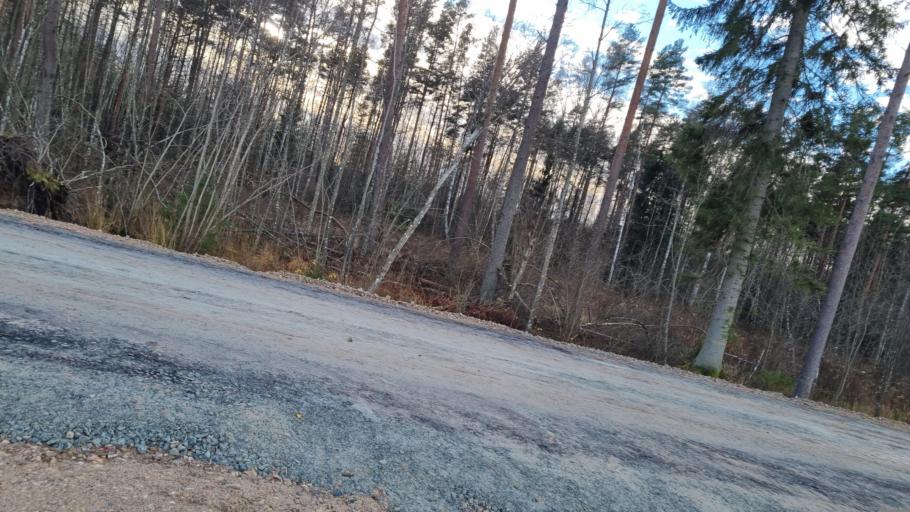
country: LV
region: Kekava
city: Kekava
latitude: 56.8075
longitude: 24.1945
